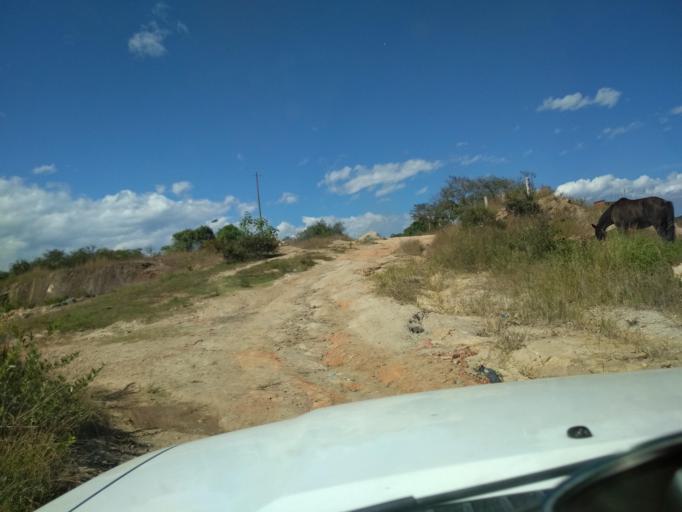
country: MX
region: Veracruz
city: El Castillo
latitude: 19.5454
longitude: -96.8528
